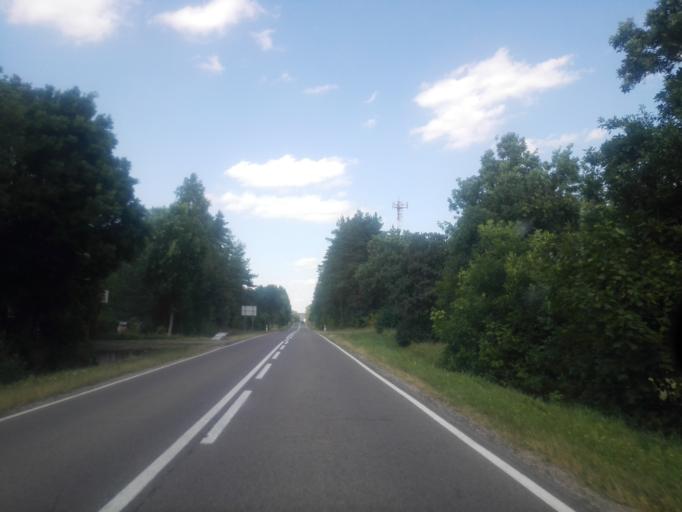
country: PL
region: Podlasie
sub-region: Powiat sejnenski
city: Sejny
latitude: 54.0289
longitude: 23.3486
